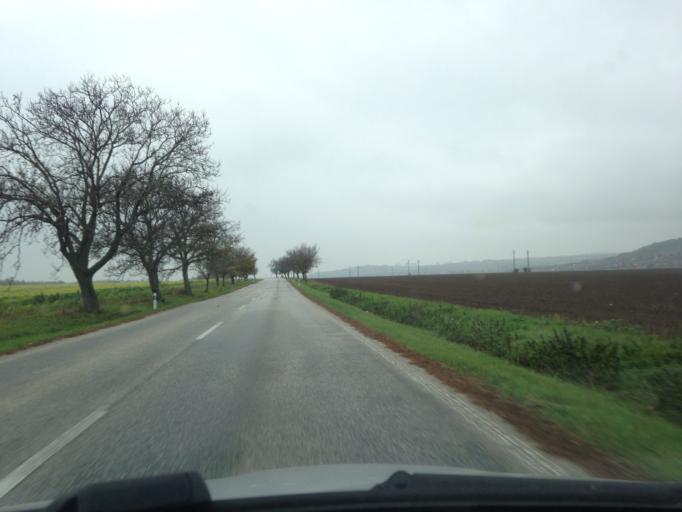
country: HU
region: Komarom-Esztergom
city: Tat
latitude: 47.8062
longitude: 18.6404
